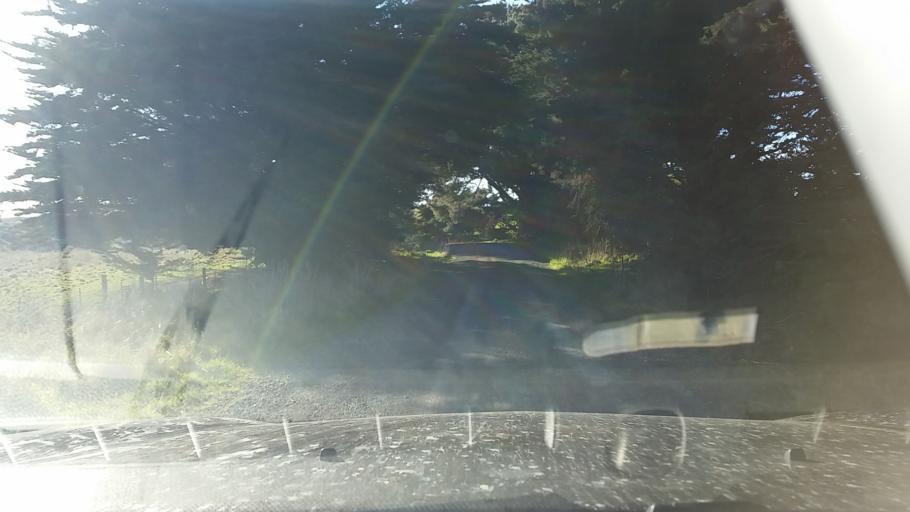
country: NZ
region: Marlborough
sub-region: Marlborough District
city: Blenheim
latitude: -41.7360
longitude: 173.9955
